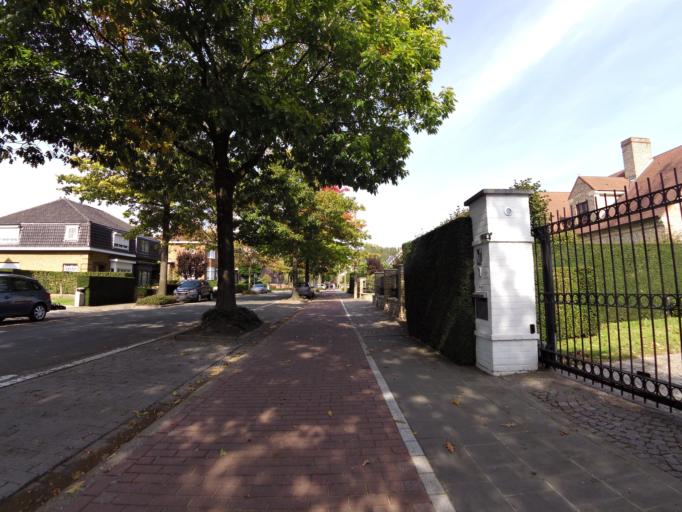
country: BE
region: Flanders
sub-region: Provincie West-Vlaanderen
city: Sint-Kruis
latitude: 51.2232
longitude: 3.2415
